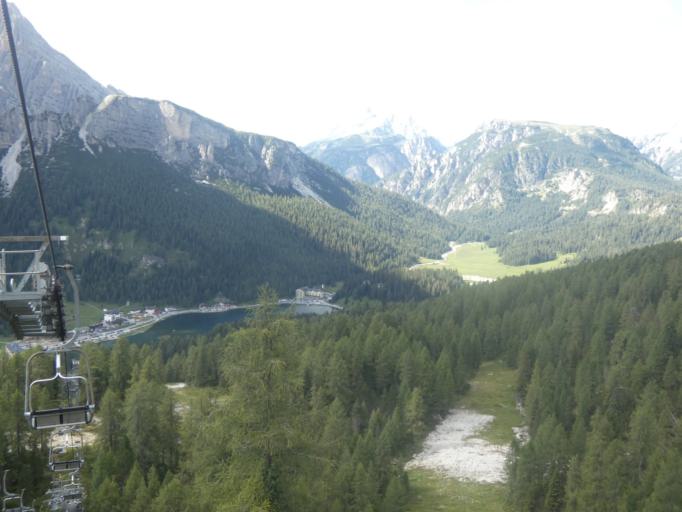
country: IT
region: Veneto
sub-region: Provincia di Belluno
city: San Vito
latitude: 46.5734
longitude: 12.2622
